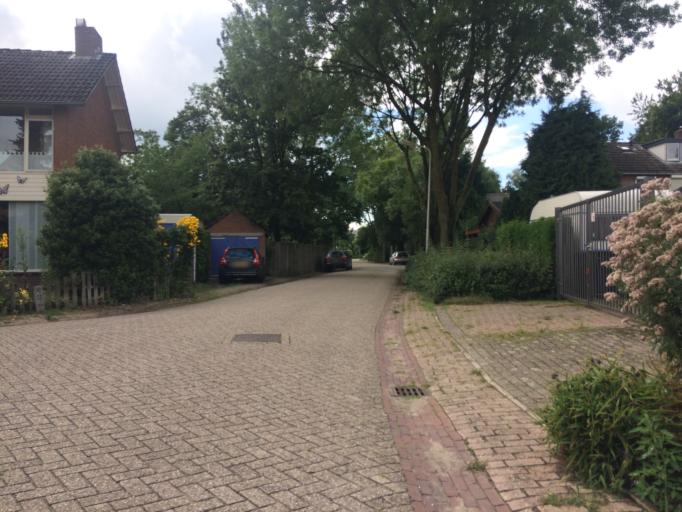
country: NL
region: Gelderland
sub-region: Gemeente Maasdriel
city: Hedel
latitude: 51.7219
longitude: 5.2679
